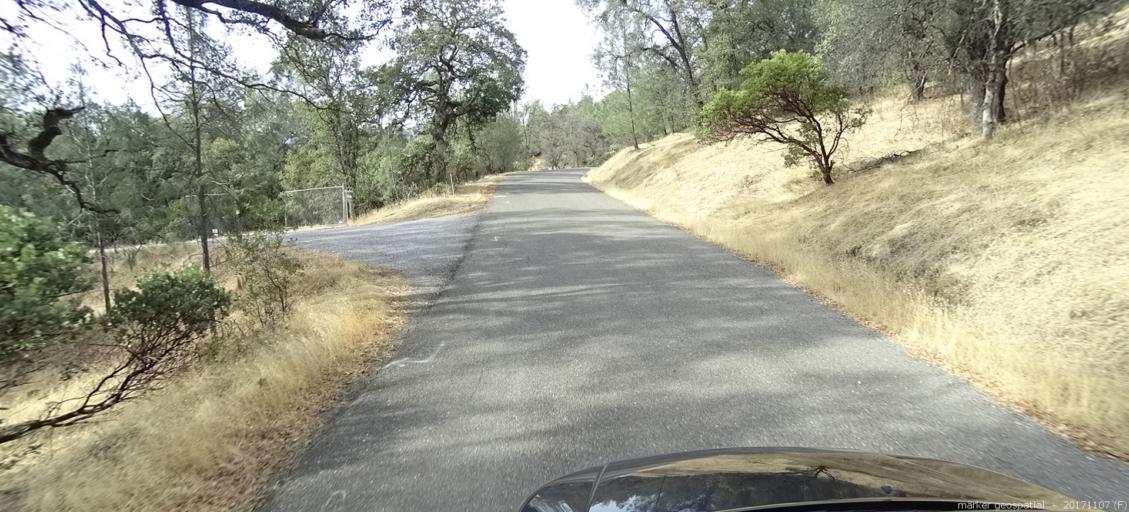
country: US
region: California
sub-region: Shasta County
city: Shasta
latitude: 40.5190
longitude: -122.5237
